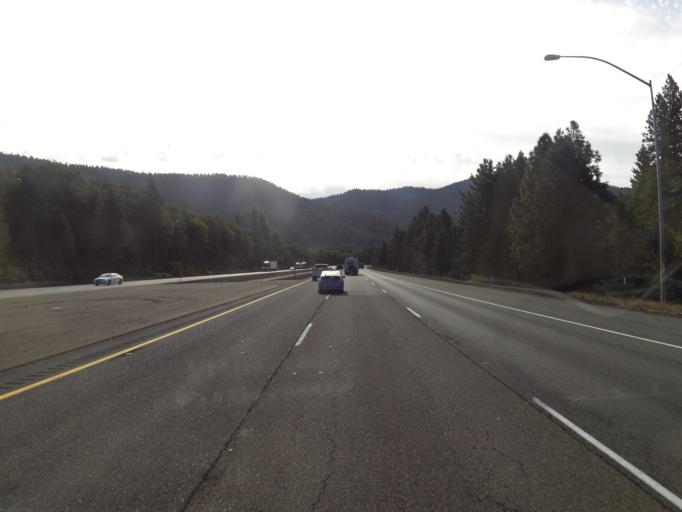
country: US
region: California
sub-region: Siskiyou County
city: Dunsmuir
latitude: 41.2548
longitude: -122.2663
